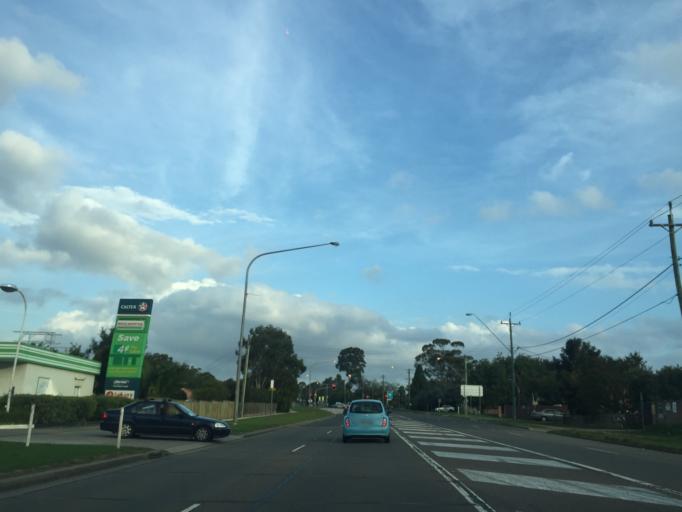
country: AU
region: New South Wales
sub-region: The Hills Shire
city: Beaumont Hills
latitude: -33.7144
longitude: 150.9599
